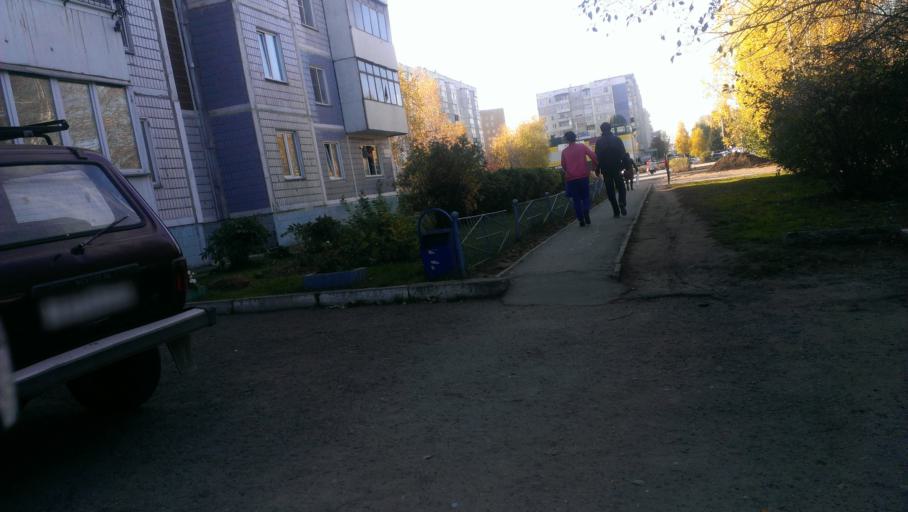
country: RU
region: Altai Krai
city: Novosilikatnyy
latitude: 53.3348
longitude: 83.6792
